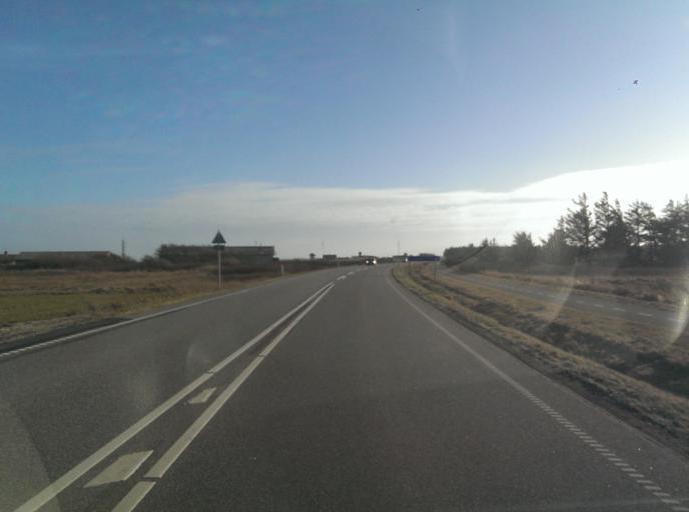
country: DK
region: Central Jutland
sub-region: Ringkobing-Skjern Kommune
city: Hvide Sande
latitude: 56.0990
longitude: 8.1282
